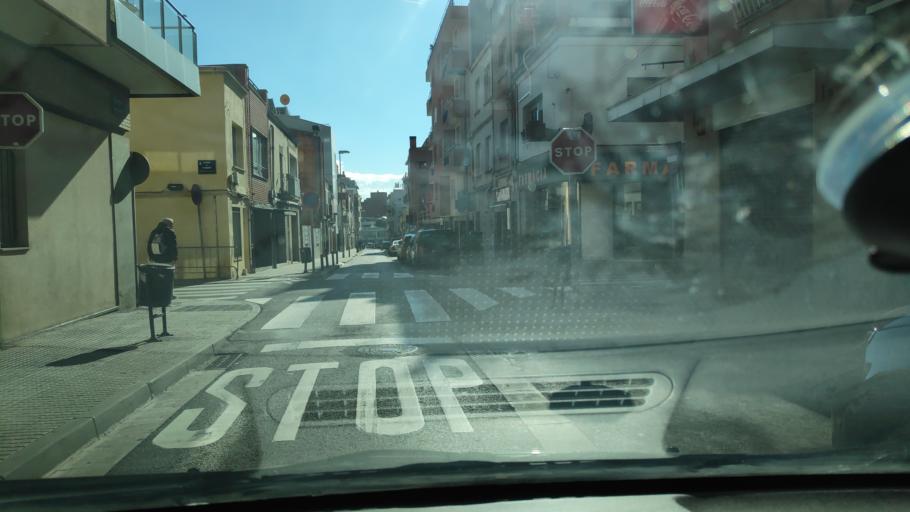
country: ES
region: Catalonia
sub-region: Provincia de Barcelona
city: Terrassa
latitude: 41.5716
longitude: 2.0182
